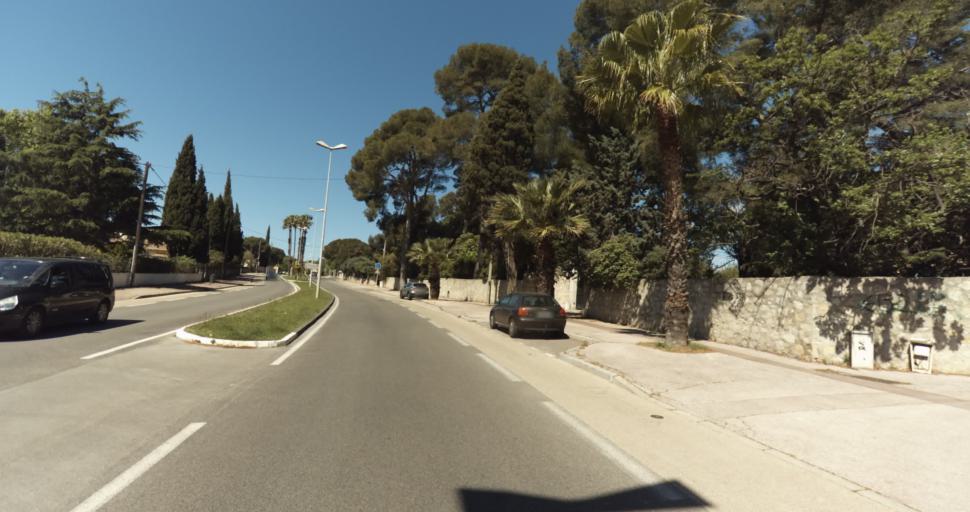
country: FR
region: Provence-Alpes-Cote d'Azur
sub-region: Departement du Var
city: La Valette-du-Var
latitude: 43.1105
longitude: 5.9716
